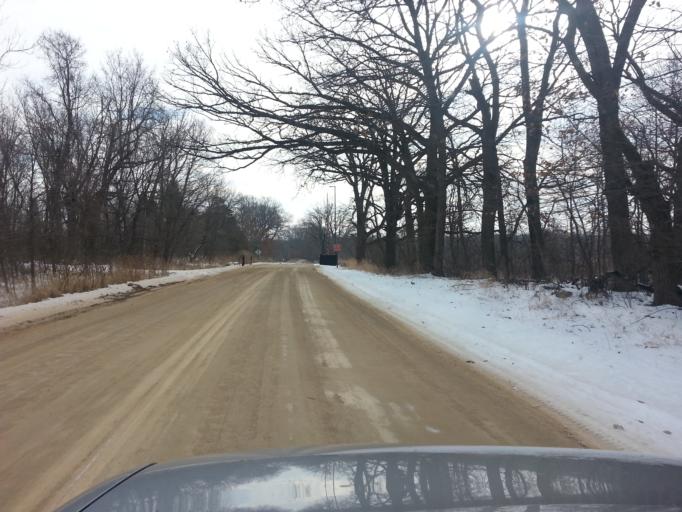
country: US
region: Minnesota
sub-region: Scott County
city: Prior Lake
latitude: 44.7185
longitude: -93.4744
